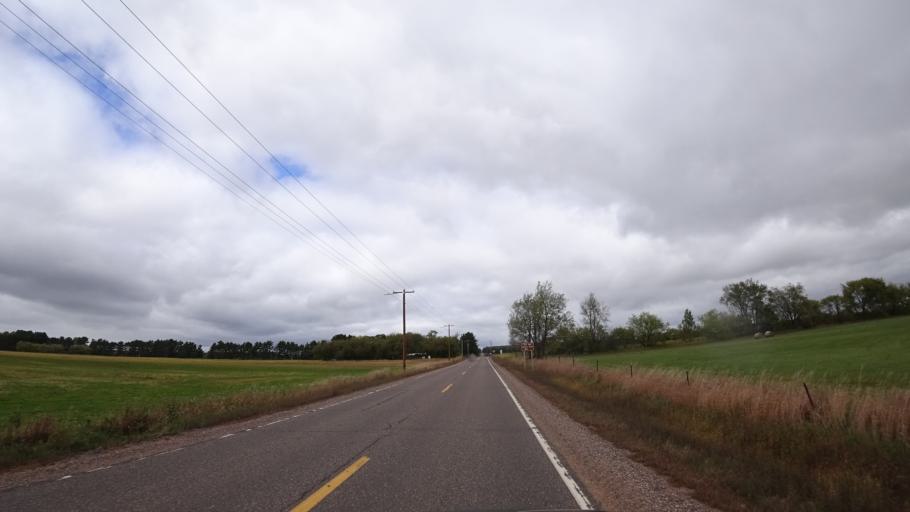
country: US
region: Wisconsin
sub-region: Chippewa County
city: Lake Wissota
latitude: 44.9777
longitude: -91.2677
